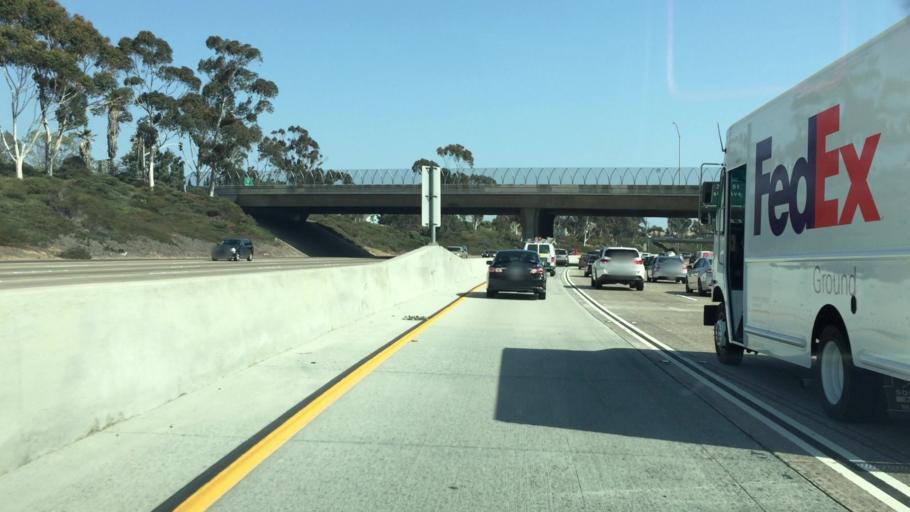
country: US
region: California
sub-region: San Diego County
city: National City
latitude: 32.7051
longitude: -117.0954
